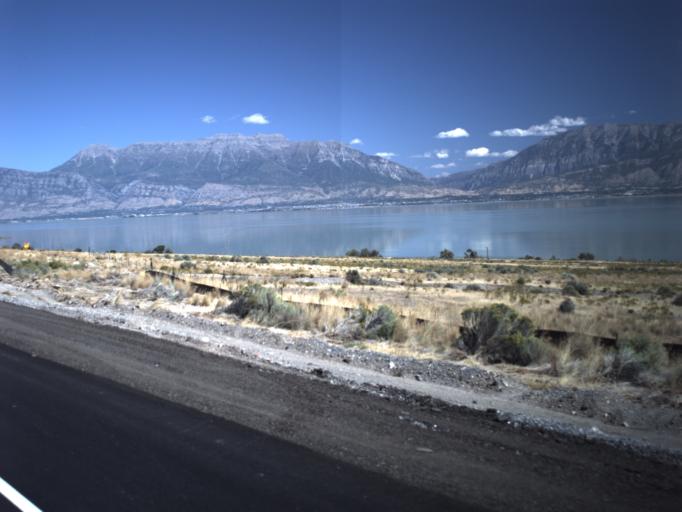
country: US
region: Utah
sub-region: Utah County
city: Saratoga Springs
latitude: 40.2349
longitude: -111.8705
